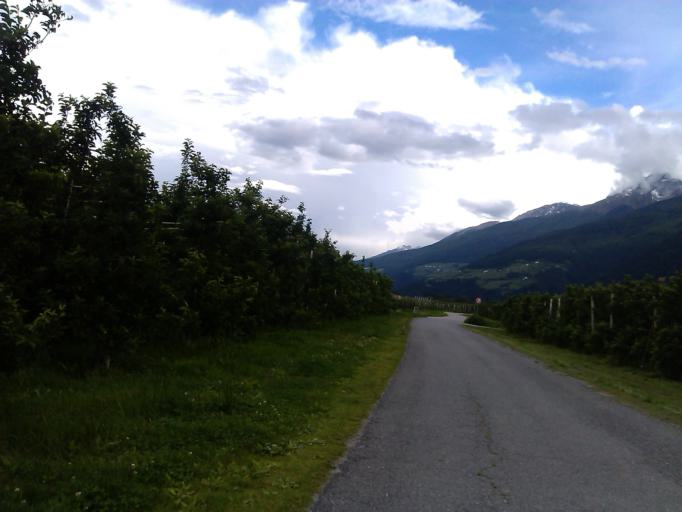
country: IT
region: Trentino-Alto Adige
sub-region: Bolzano
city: Prato Allo Stelvio
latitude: 46.6277
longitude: 10.6186
